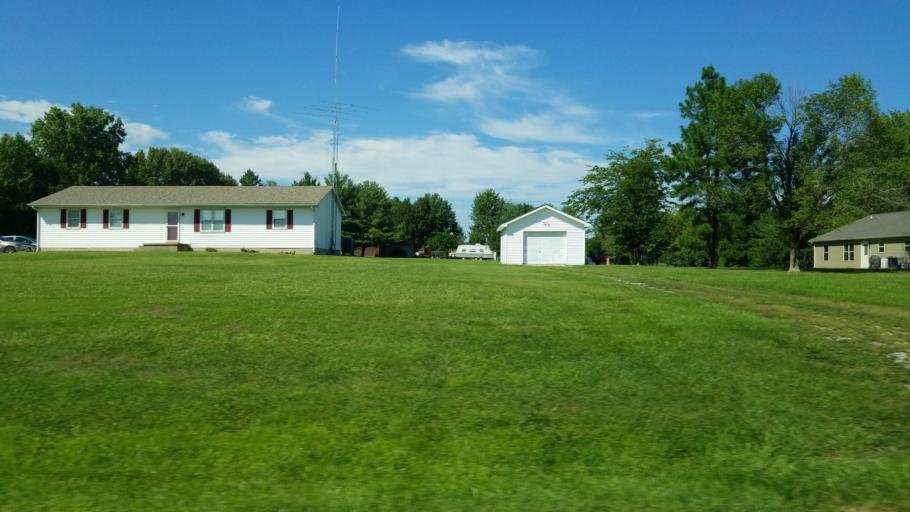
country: US
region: Illinois
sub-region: Williamson County
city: Marion
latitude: 37.7446
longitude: -88.8809
